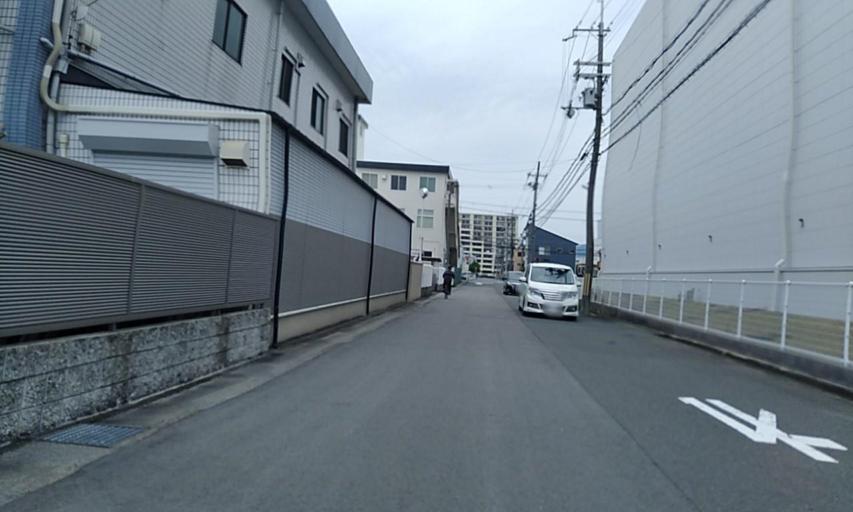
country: JP
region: Kyoto
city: Muko
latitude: 34.9414
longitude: 135.7500
